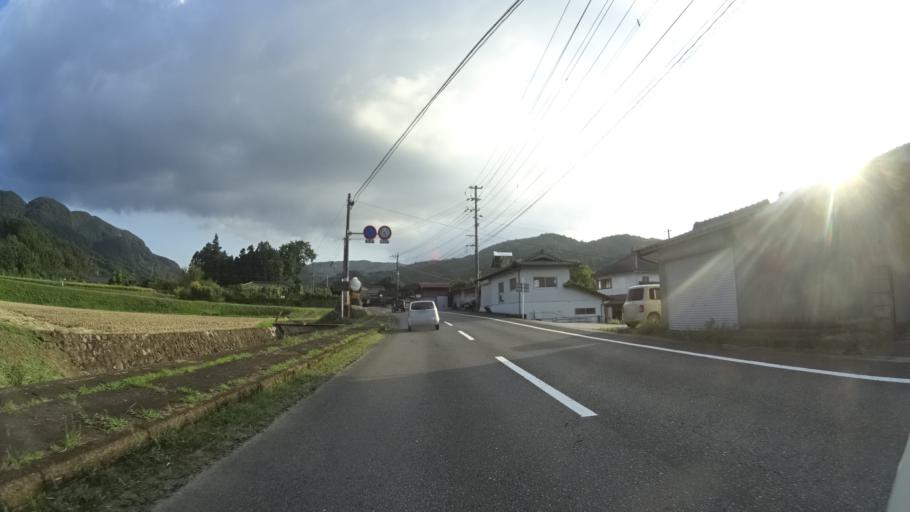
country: JP
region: Oita
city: Hiji
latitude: 33.3789
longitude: 131.3961
